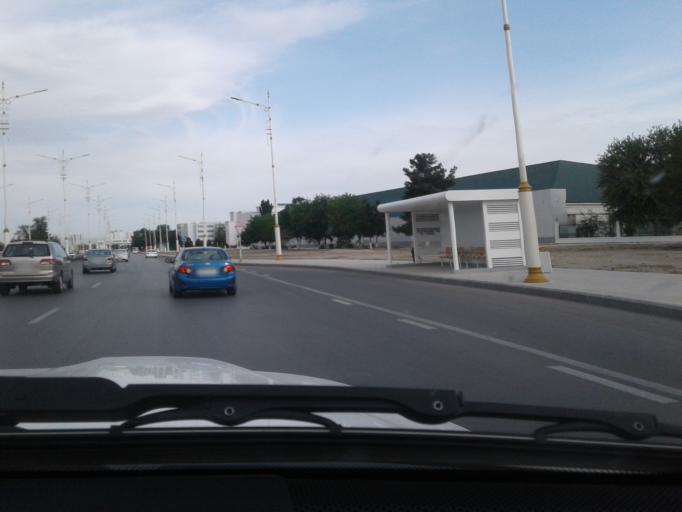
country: TM
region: Ahal
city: Ashgabat
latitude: 37.9593
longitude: 58.3660
